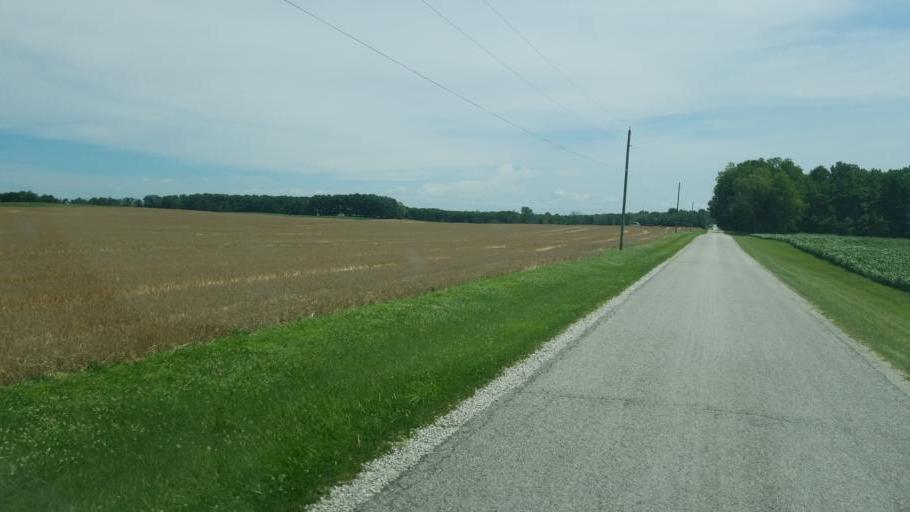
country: US
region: Ohio
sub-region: Crawford County
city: Bucyrus
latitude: 40.8709
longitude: -82.8926
